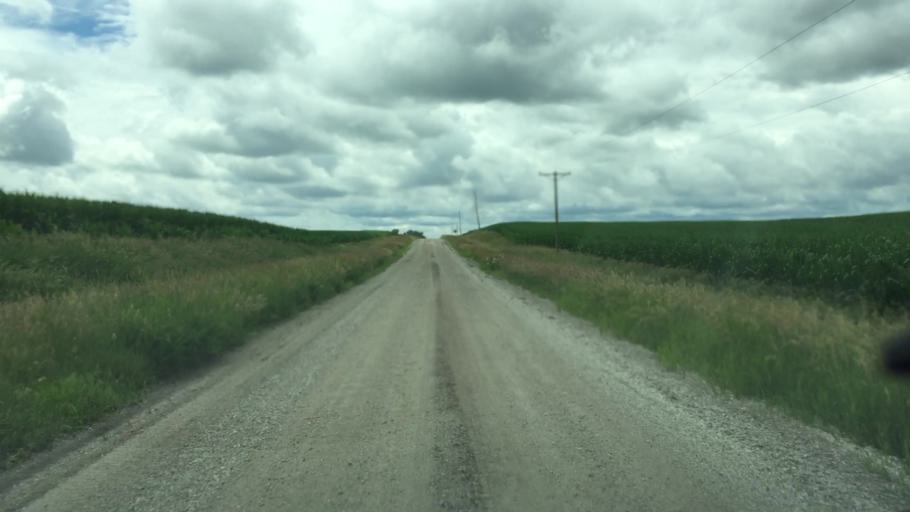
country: US
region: Iowa
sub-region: Jasper County
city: Prairie City
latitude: 41.5848
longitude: -93.1596
